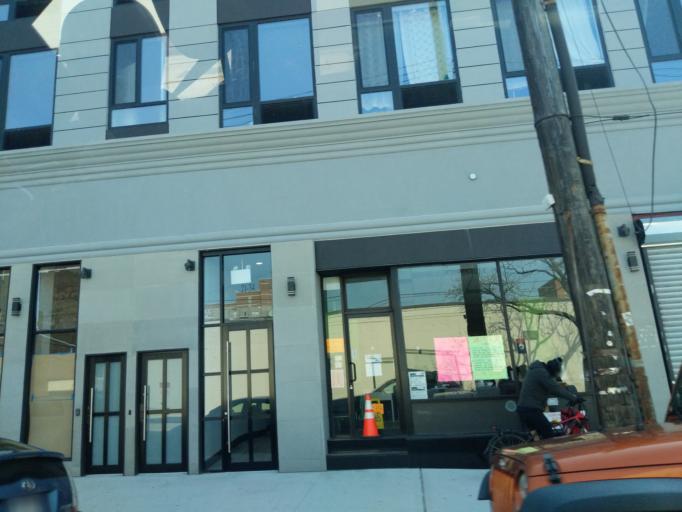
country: US
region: New York
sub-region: Queens County
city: Long Island City
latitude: 40.7646
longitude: -73.9306
